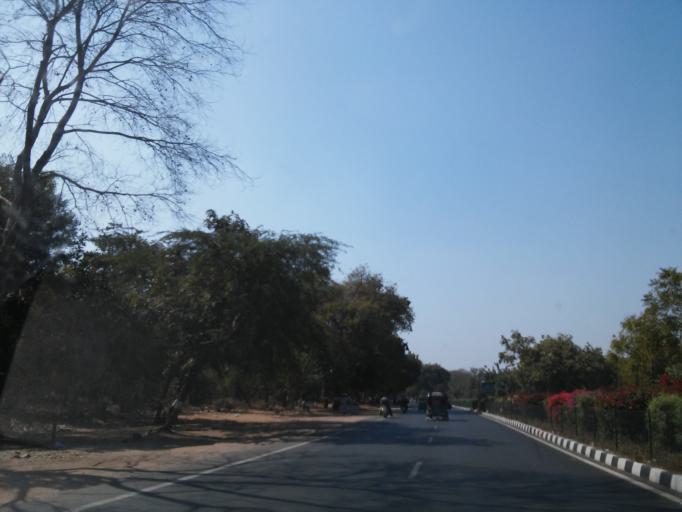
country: IN
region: Gujarat
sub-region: Gandhinagar
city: Ghandinagar
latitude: 23.1973
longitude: 72.6300
